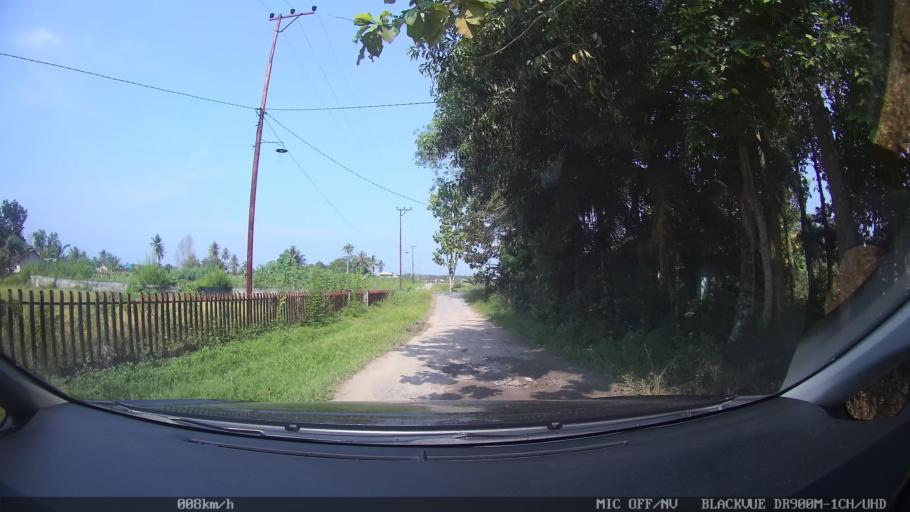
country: ID
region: Lampung
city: Natar
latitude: -5.2545
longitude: 105.1866
